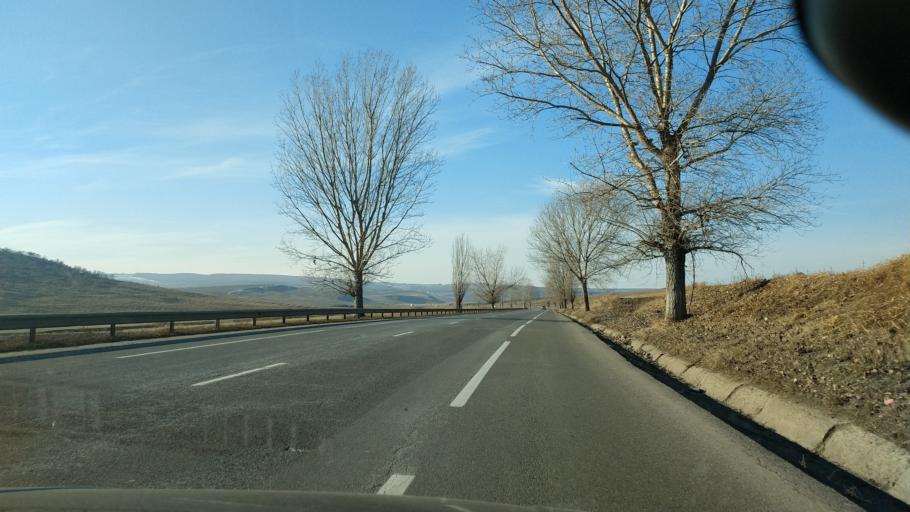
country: RO
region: Iasi
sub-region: Comuna Targu Frumos
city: Targu Frumos
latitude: 47.1970
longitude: 26.9866
